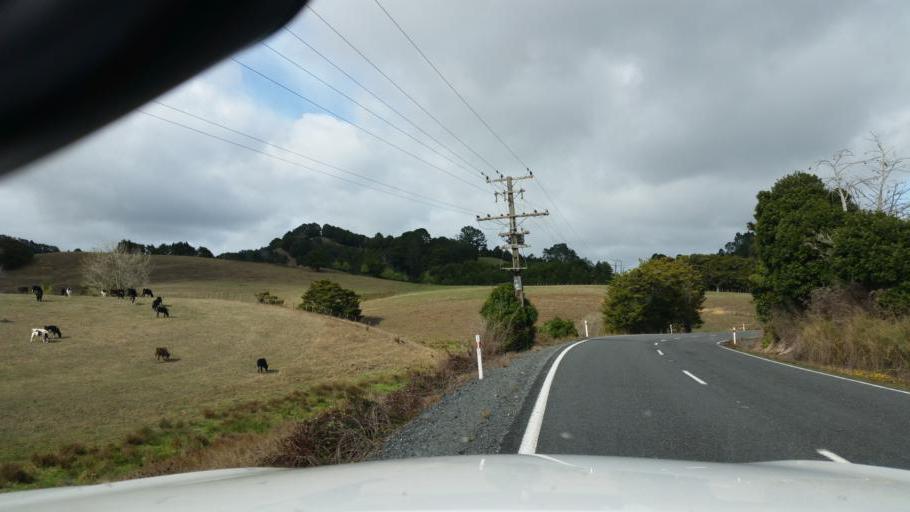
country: NZ
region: Northland
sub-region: Whangarei
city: Ruakaka
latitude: -36.0257
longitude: 174.2785
